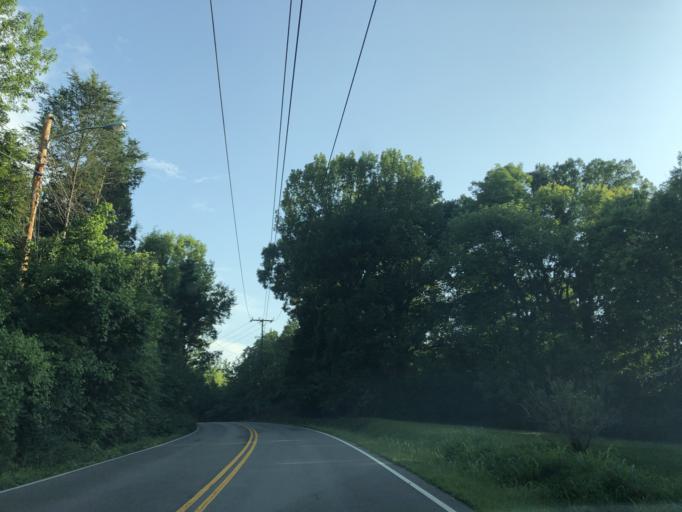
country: US
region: Tennessee
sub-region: Davidson County
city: Lakewood
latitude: 36.1514
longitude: -86.6467
